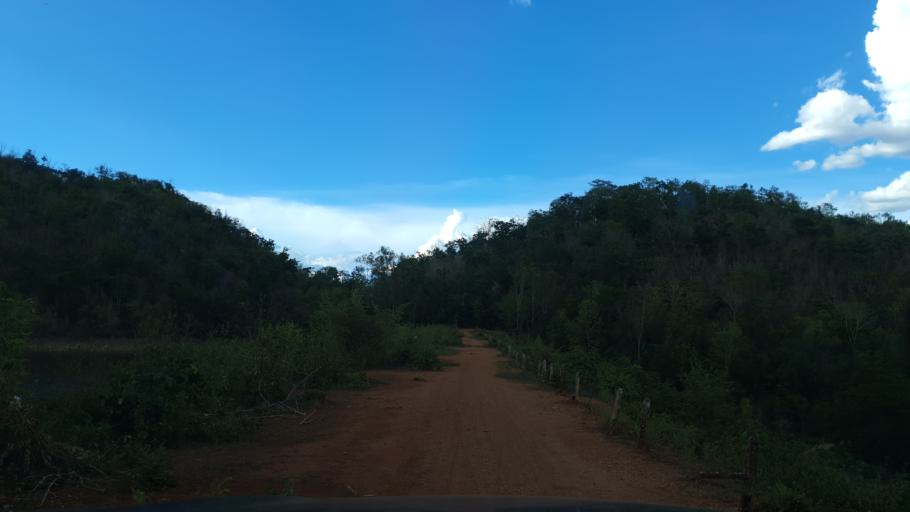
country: TH
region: Lampang
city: Sop Prap
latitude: 17.8881
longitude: 99.2839
